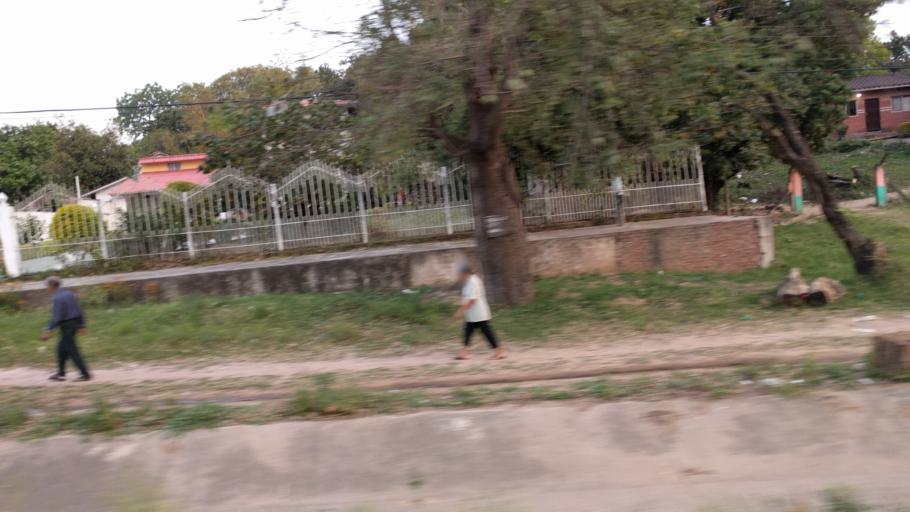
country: BO
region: Santa Cruz
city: Santa Rita
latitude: -17.8939
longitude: -63.3339
